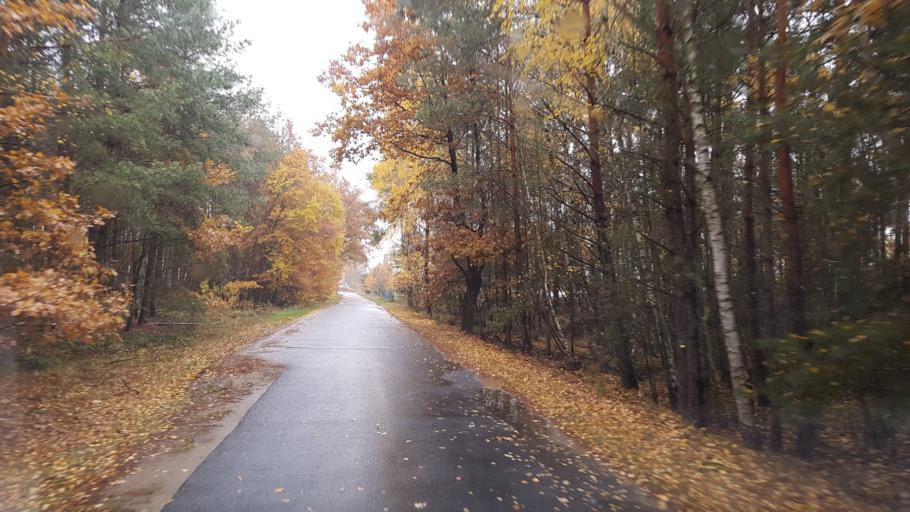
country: DE
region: Brandenburg
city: Herzberg
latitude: 51.6446
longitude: 13.2167
